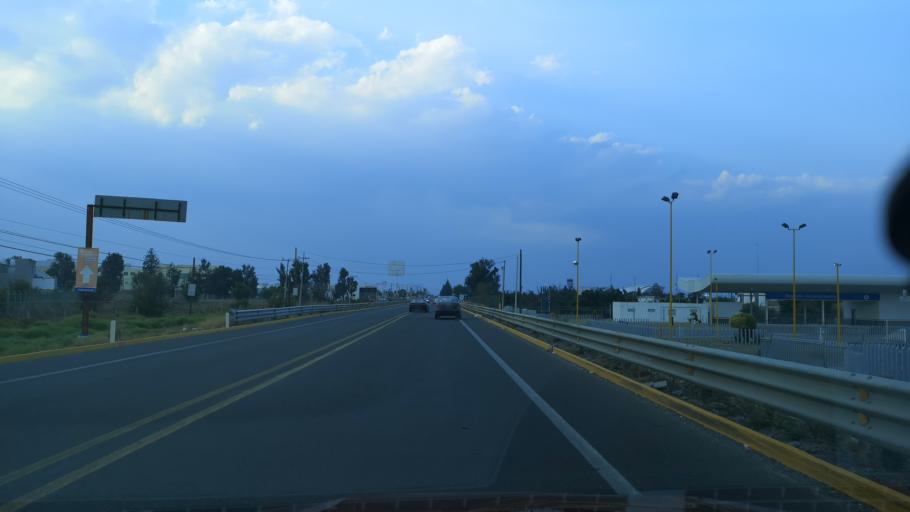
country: MX
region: Puebla
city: Huejotzingo
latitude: 19.1570
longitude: -98.3772
